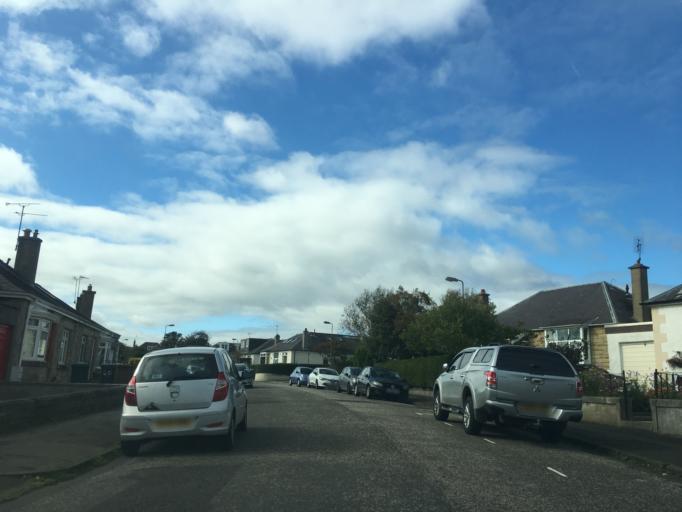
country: GB
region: Scotland
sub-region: West Lothian
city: Seafield
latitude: 55.9354
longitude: -3.1612
